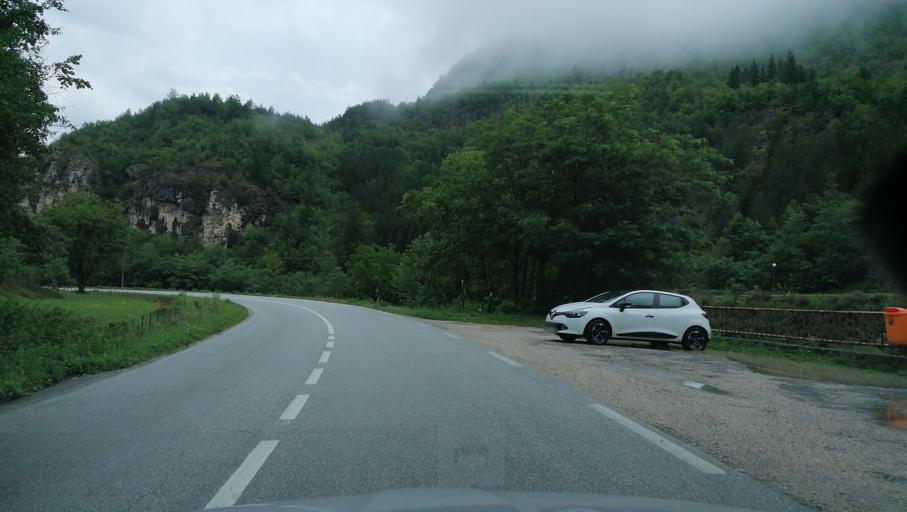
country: RS
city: Durici
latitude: 43.7559
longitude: 19.3967
